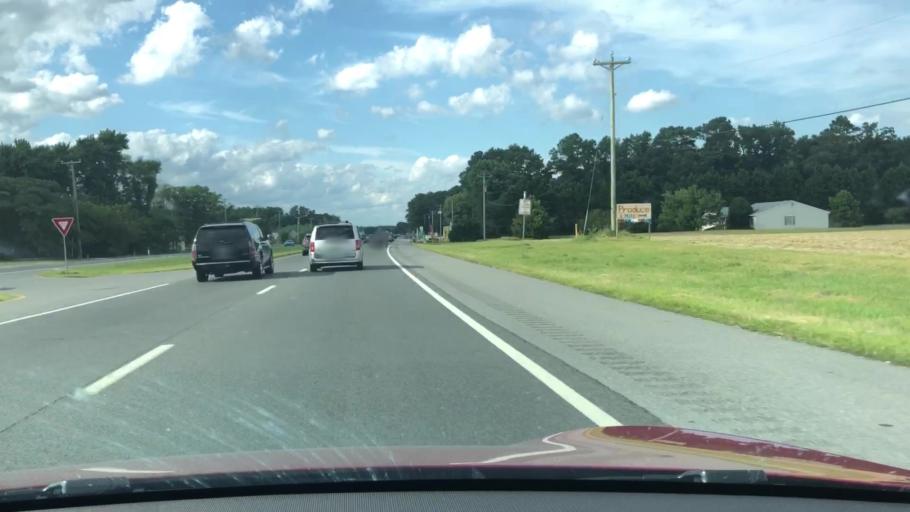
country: US
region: Delaware
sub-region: Sussex County
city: Bridgeville
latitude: 38.8119
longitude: -75.5849
